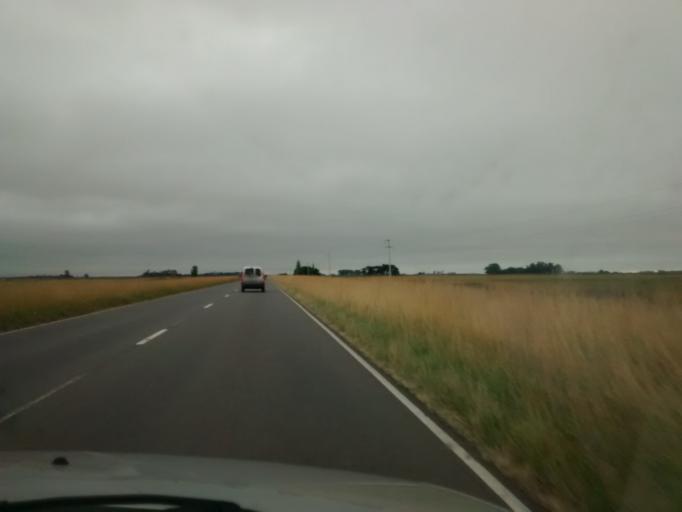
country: AR
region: Buenos Aires
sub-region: Partido de Ayacucho
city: Ayacucho
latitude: -37.0241
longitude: -58.5389
